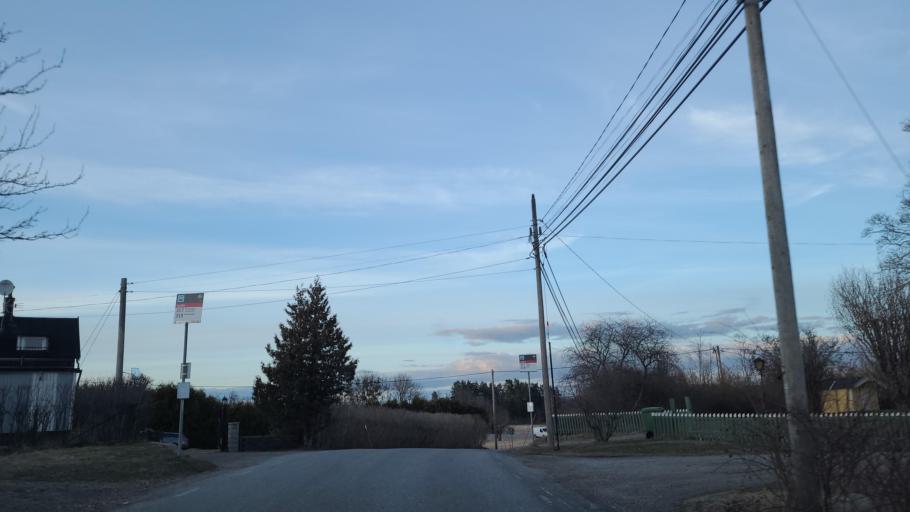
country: SE
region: Stockholm
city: Stenhamra
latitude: 59.3983
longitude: 17.6559
